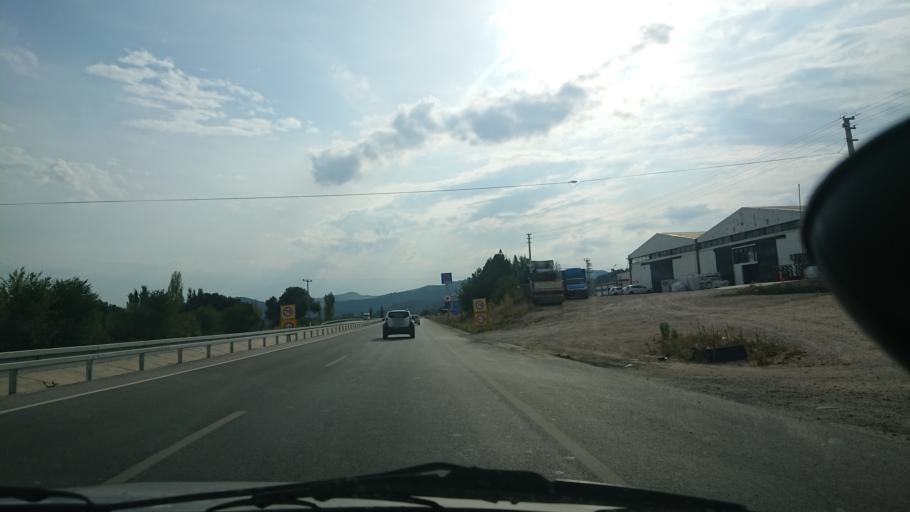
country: TR
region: Kuetahya
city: Gediz
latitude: 38.9380
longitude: 29.3171
